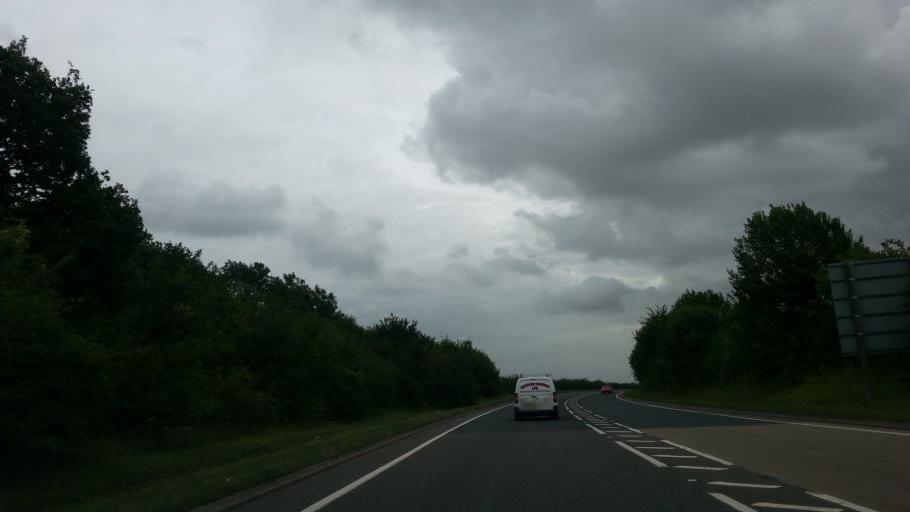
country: GB
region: England
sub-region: Essex
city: Chelmsford
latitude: 51.7965
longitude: 0.4825
